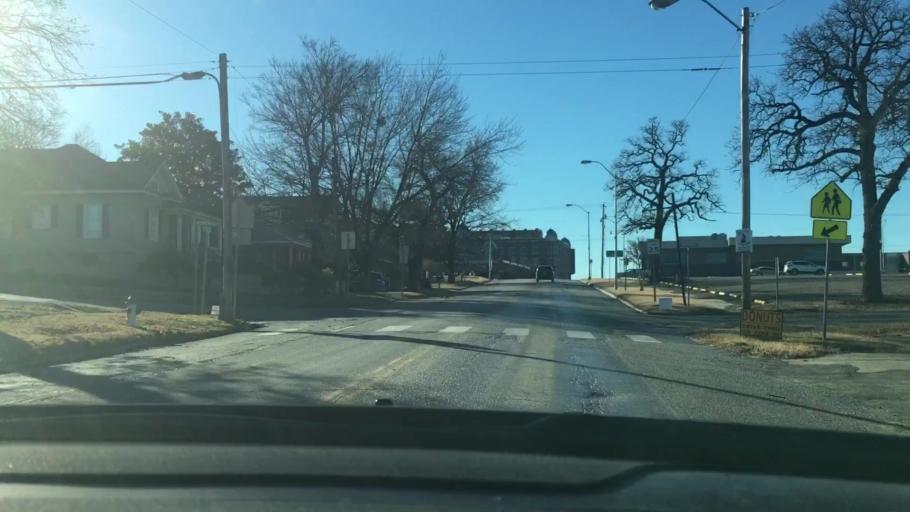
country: US
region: Oklahoma
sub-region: Murray County
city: Sulphur
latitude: 34.5102
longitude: -96.9684
